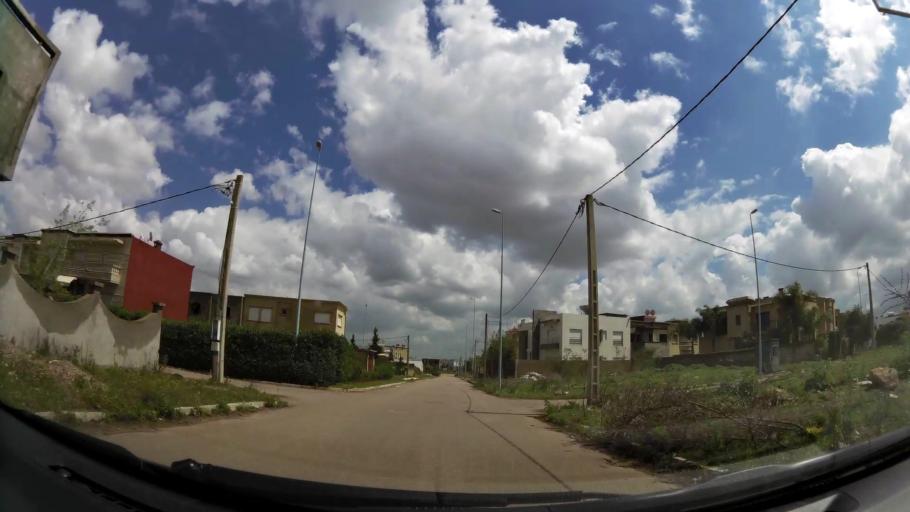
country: MA
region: Chaouia-Ouardigha
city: Nouaseur
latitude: 33.3971
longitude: -7.5656
